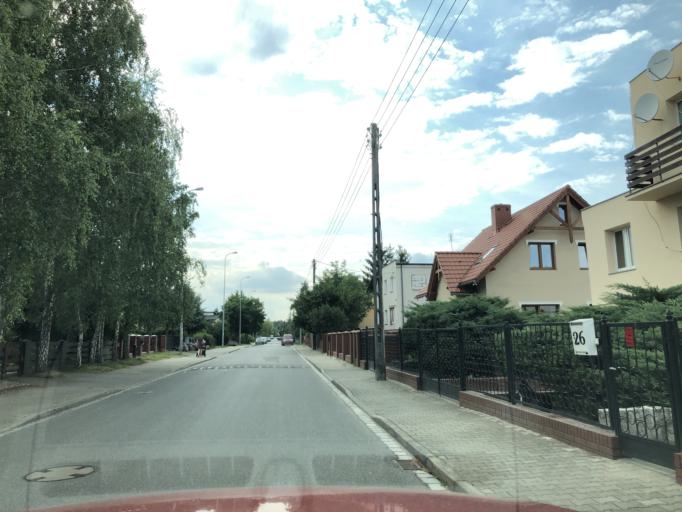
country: PL
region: Lower Silesian Voivodeship
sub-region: Powiat wroclawski
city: Smolec
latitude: 51.1568
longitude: 16.9029
